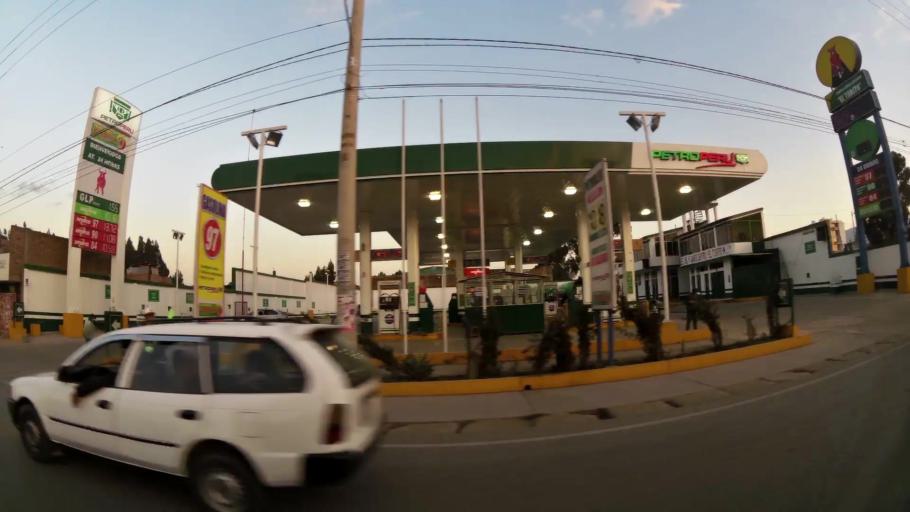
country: PE
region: Junin
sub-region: Provincia de Huancayo
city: Pilcomay
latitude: -12.0527
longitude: -75.2416
